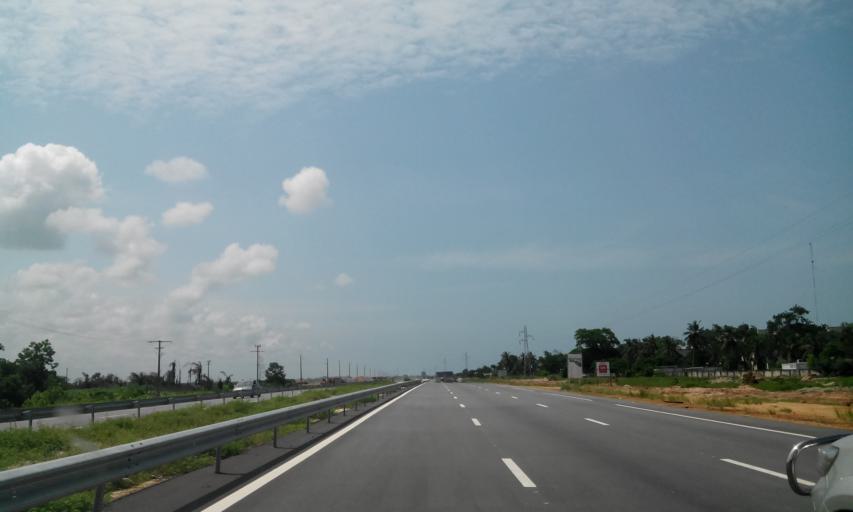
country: CI
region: Sud-Comoe
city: Grand-Bassam
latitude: 5.2325
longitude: -3.7621
